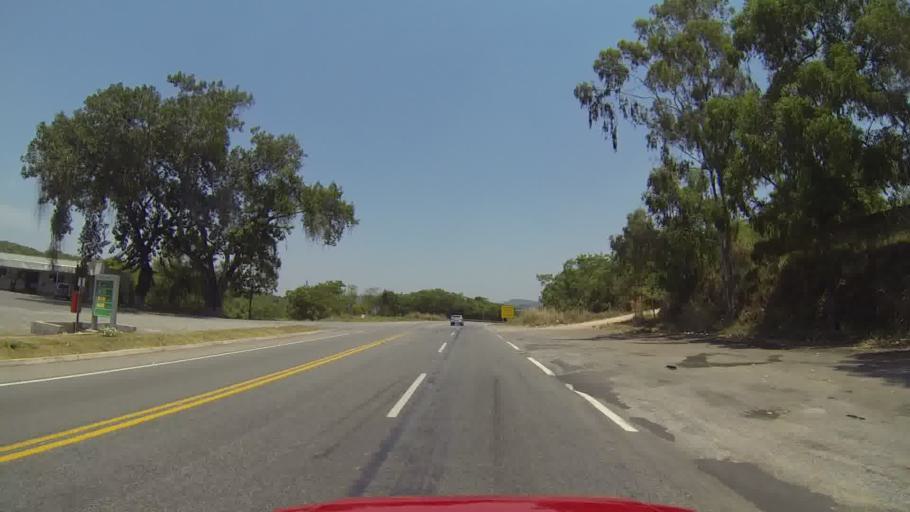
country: BR
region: Minas Gerais
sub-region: Itapecerica
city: Itapecerica
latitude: -20.2797
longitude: -45.1303
